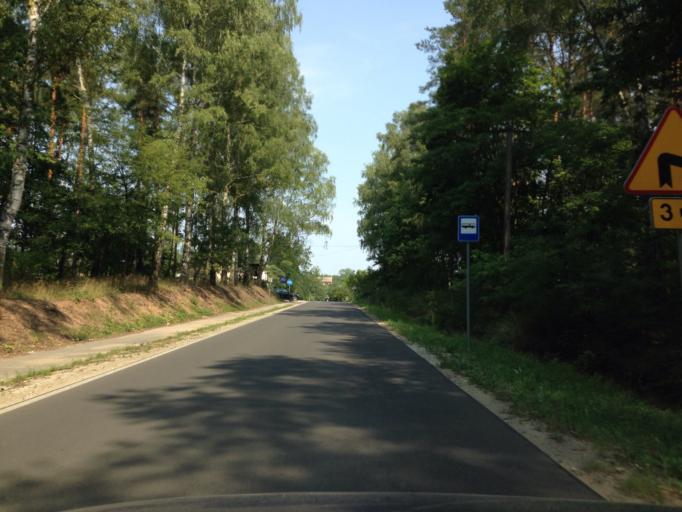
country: PL
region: Kujawsko-Pomorskie
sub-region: Powiat golubsko-dobrzynski
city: Golub-Dobrzyn
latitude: 53.0929
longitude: 19.0389
